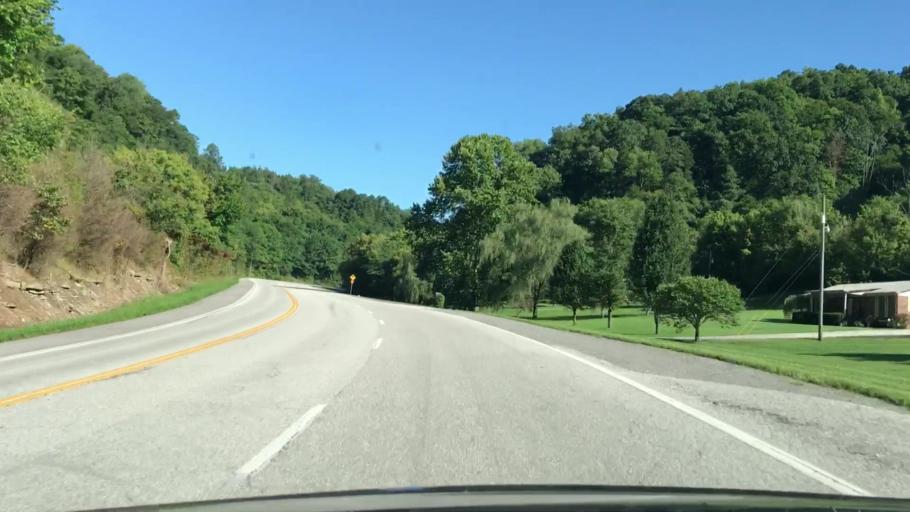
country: US
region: Tennessee
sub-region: Clay County
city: Celina
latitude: 36.5040
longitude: -85.5477
